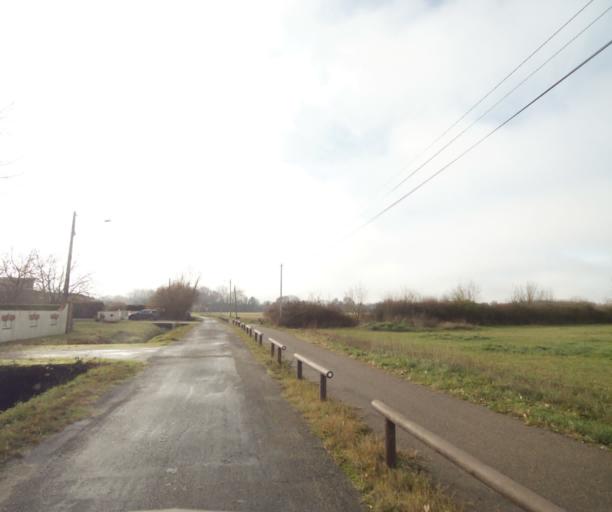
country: FR
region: Midi-Pyrenees
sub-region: Departement de la Haute-Garonne
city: Villemur-sur-Tarn
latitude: 43.8570
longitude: 1.4985
